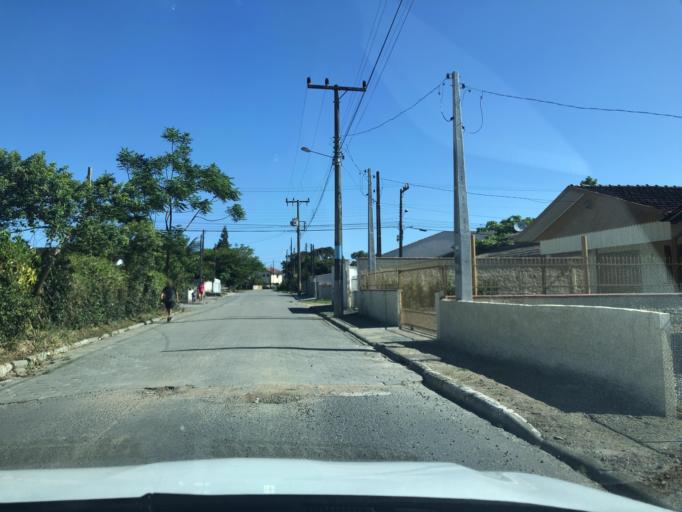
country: BR
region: Santa Catarina
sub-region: Sao Francisco Do Sul
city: Sao Francisco do Sul
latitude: -26.2285
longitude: -48.5193
